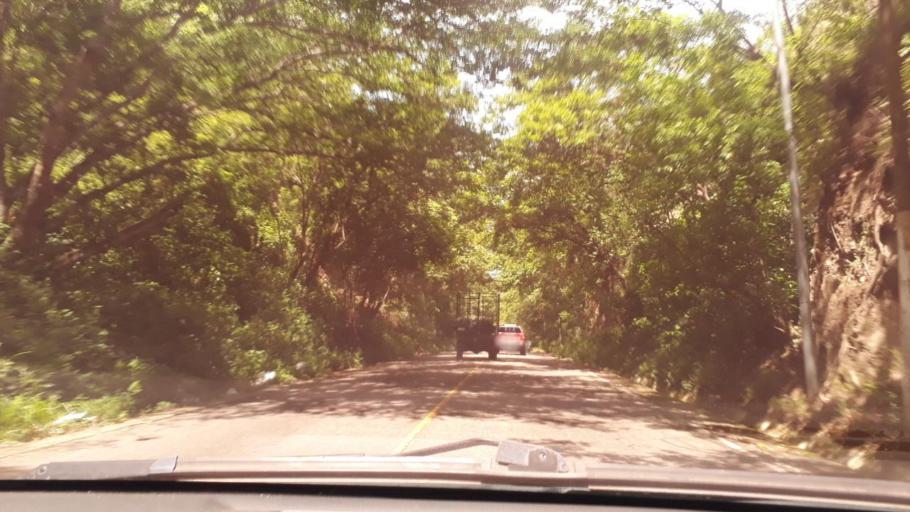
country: GT
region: Jutiapa
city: Jalpatagua
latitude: 14.1621
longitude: -90.0516
